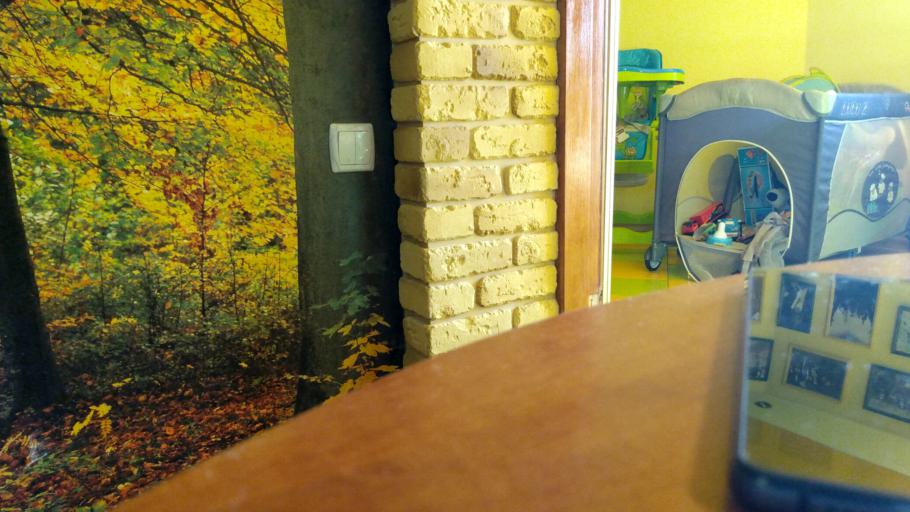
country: RU
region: Tverskaya
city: Likhoslavl'
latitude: 57.1854
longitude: 35.5450
